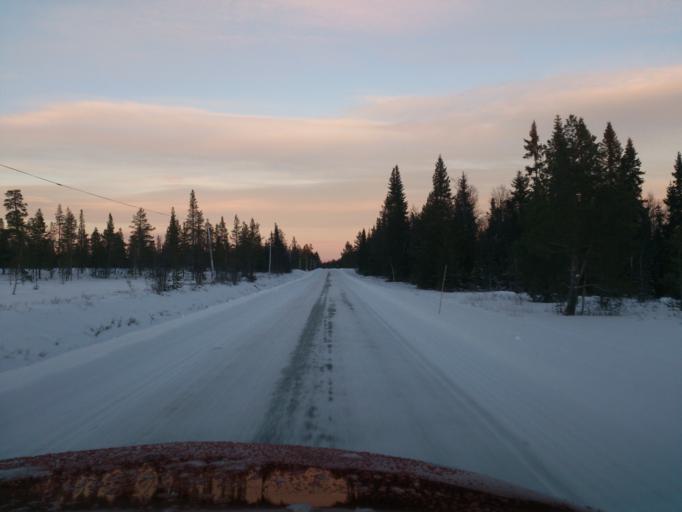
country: SE
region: Jaemtland
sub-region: Harjedalens Kommun
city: Sveg
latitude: 62.3279
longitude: 13.4217
